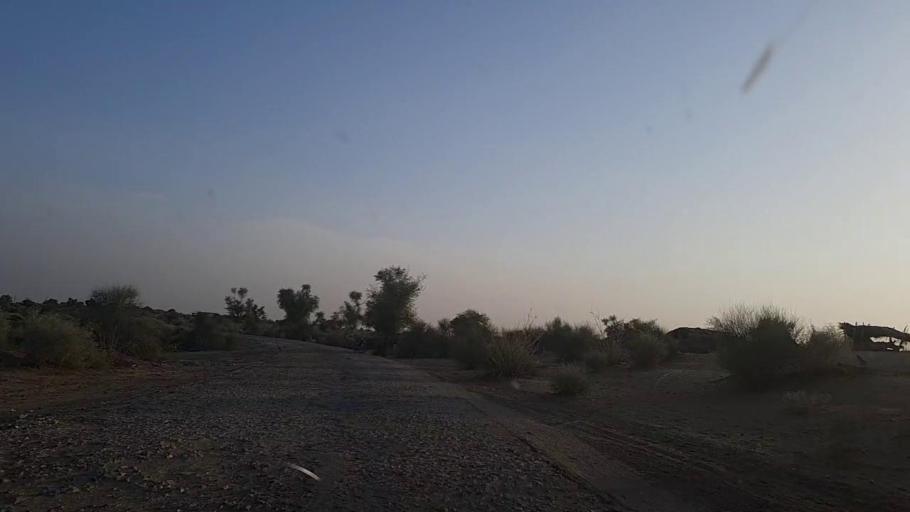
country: PK
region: Sindh
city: Khanpur
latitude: 27.6302
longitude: 69.4452
